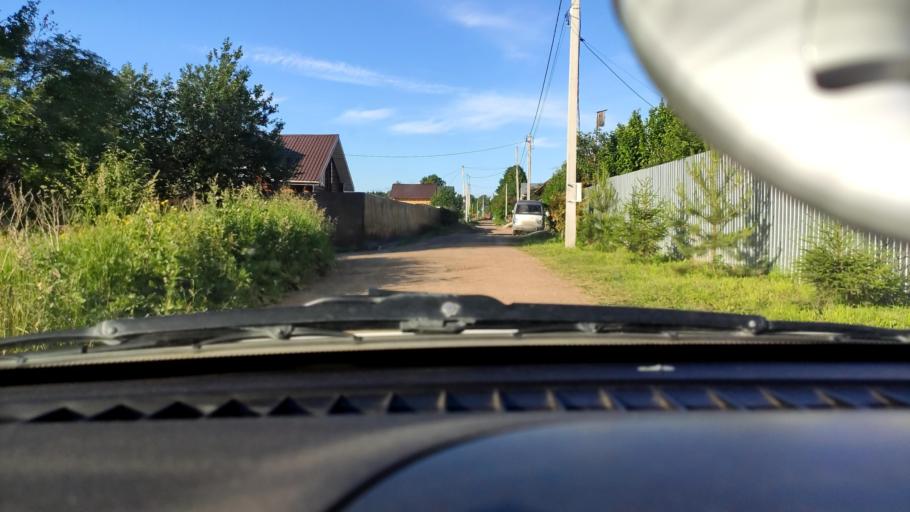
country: RU
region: Perm
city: Ferma
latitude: 57.9169
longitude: 56.3288
